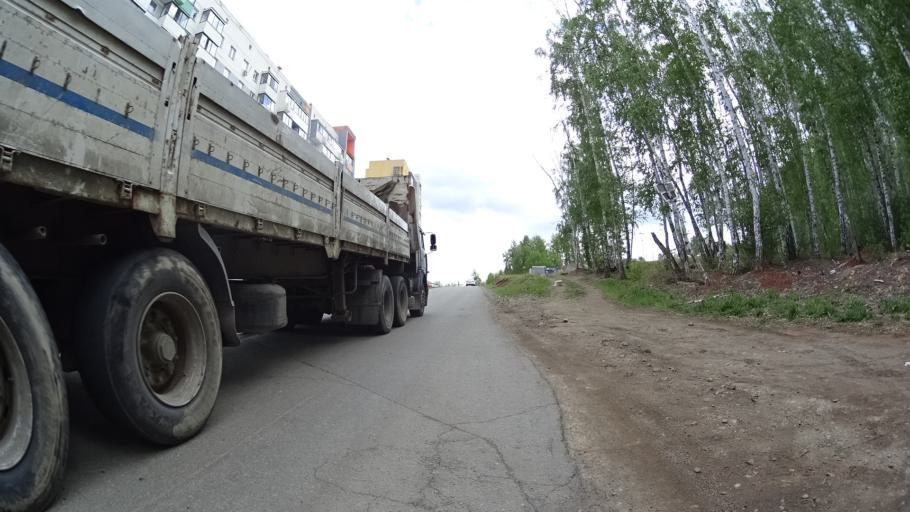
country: RU
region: Chelyabinsk
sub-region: Gorod Chelyabinsk
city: Chelyabinsk
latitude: 55.1618
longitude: 61.2857
